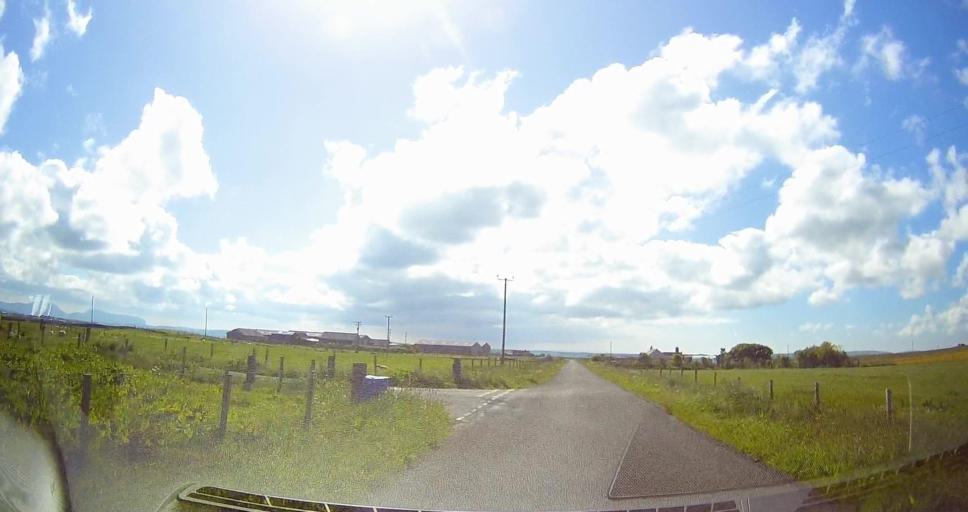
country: GB
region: Scotland
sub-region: Orkney Islands
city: Stromness
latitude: 59.0466
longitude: -3.1484
